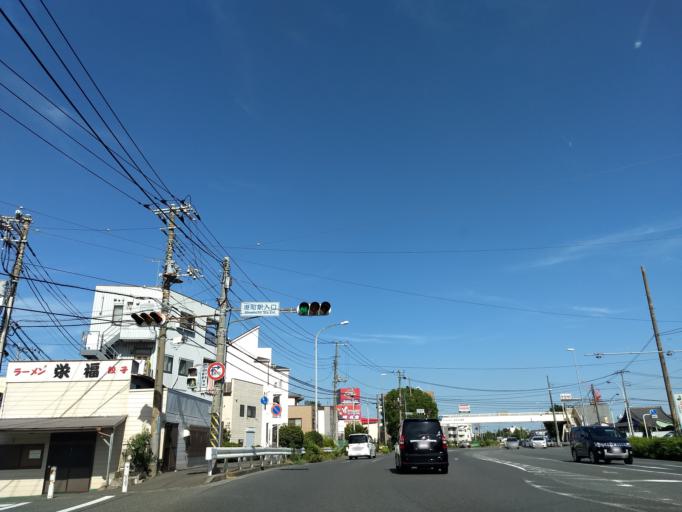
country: JP
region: Kanagawa
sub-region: Kawasaki-shi
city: Kawasaki
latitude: 35.5343
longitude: 139.7135
